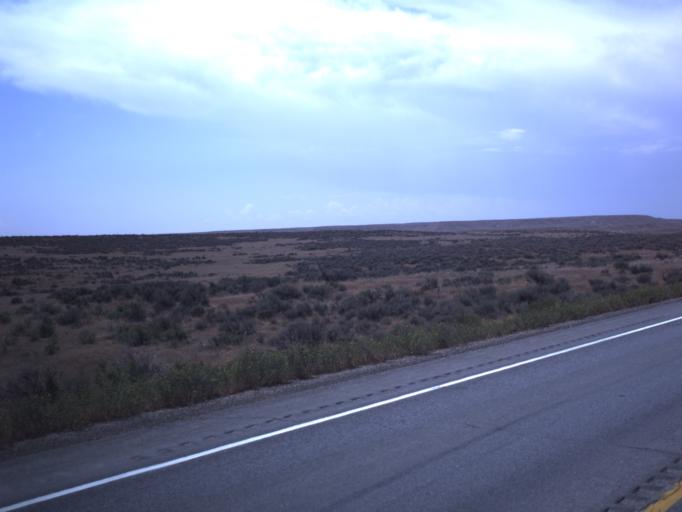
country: US
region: Utah
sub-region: Uintah County
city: Maeser
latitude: 40.3280
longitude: -109.6696
